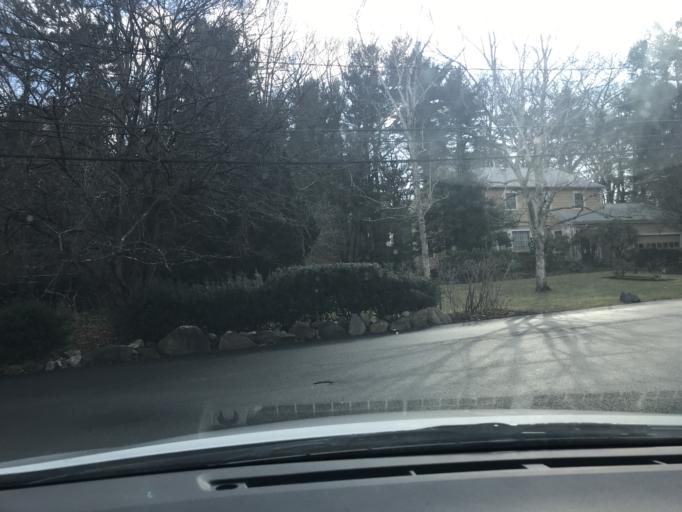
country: US
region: Massachusetts
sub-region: Middlesex County
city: Lexington
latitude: 42.4696
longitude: -71.2235
